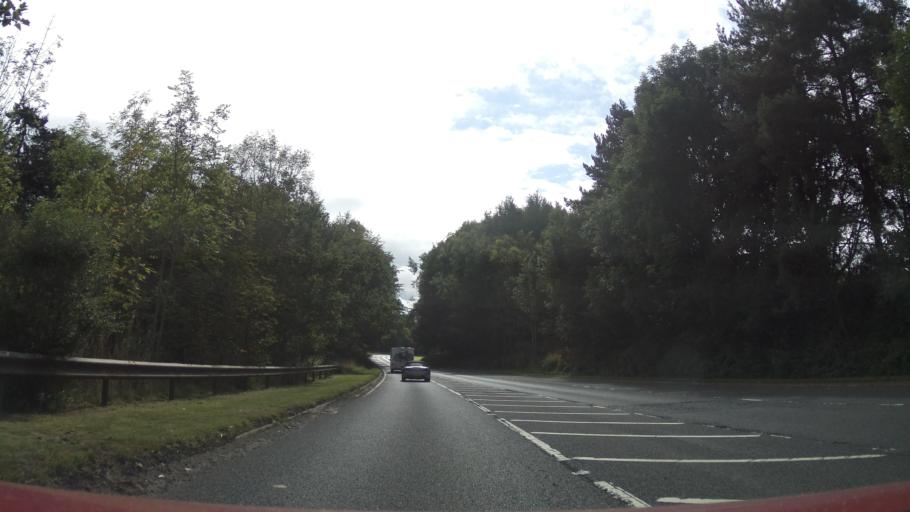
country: GB
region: Scotland
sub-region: The Scottish Borders
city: Newtown St Boswells
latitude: 55.6021
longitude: -2.6739
